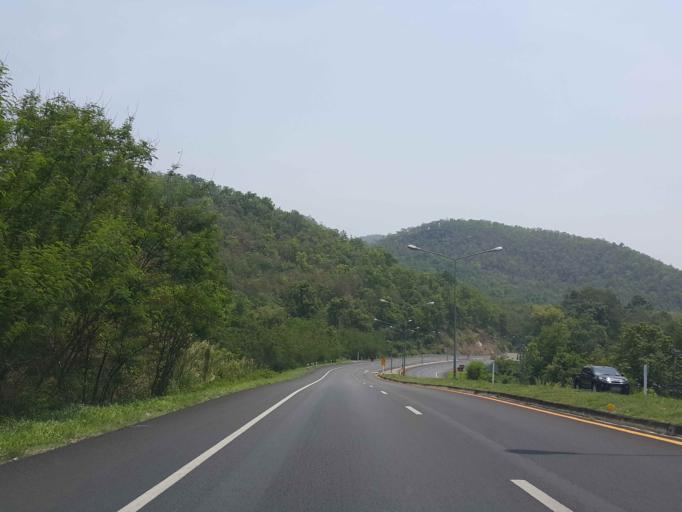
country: TH
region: Chiang Mai
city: San Sai
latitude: 18.8908
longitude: 99.1673
